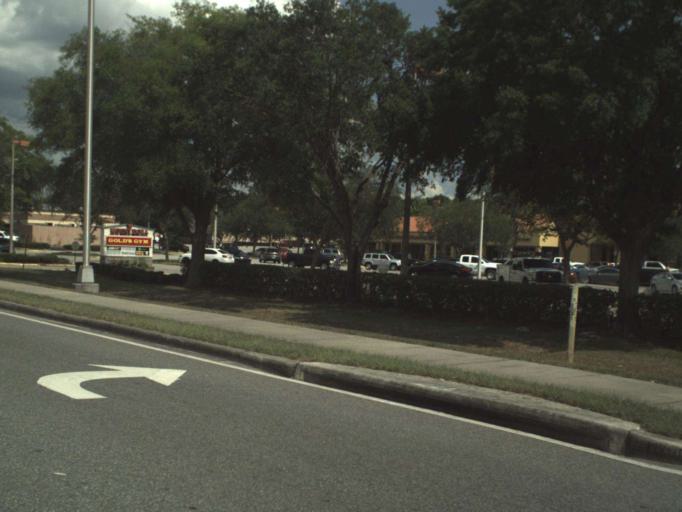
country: US
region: Florida
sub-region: Lake County
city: Mount Dora
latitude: 28.8240
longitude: -81.6456
